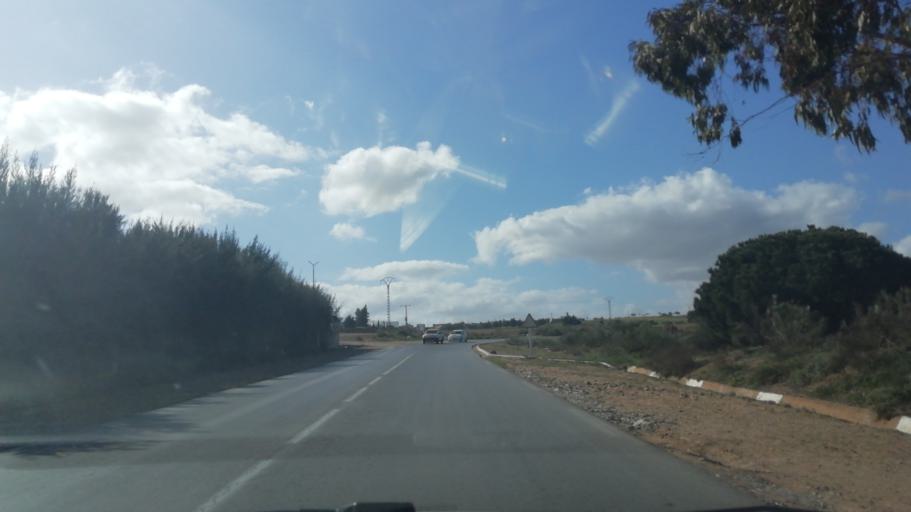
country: DZ
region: Relizane
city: Mazouna
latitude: 36.2937
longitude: 0.6559
